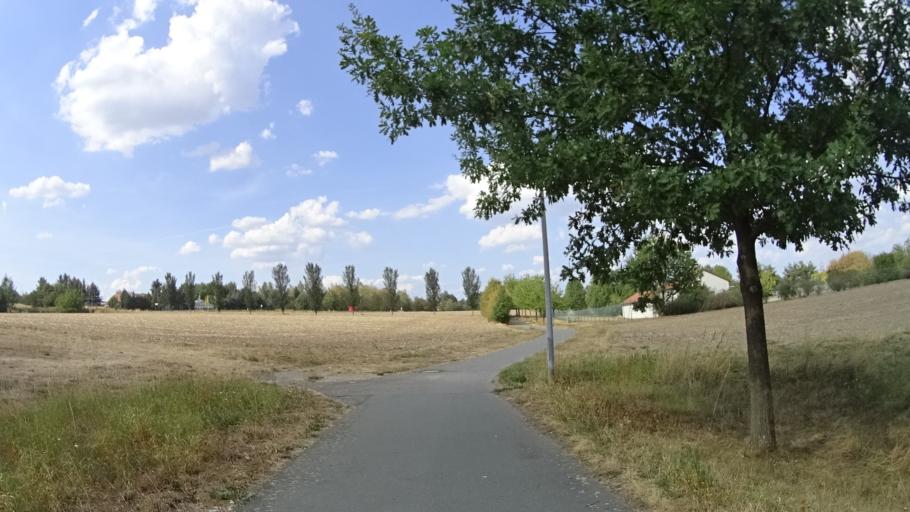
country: DE
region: Saxony
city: Ostritz
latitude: 51.0257
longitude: 14.9349
